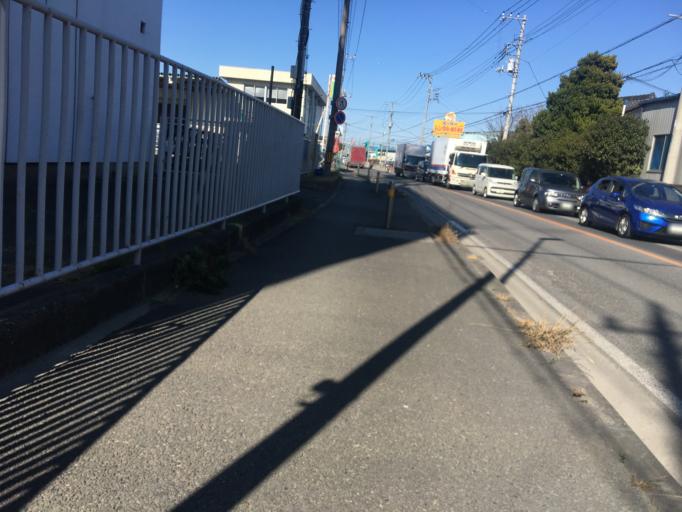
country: JP
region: Saitama
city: Asaka
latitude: 35.8223
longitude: 139.6099
